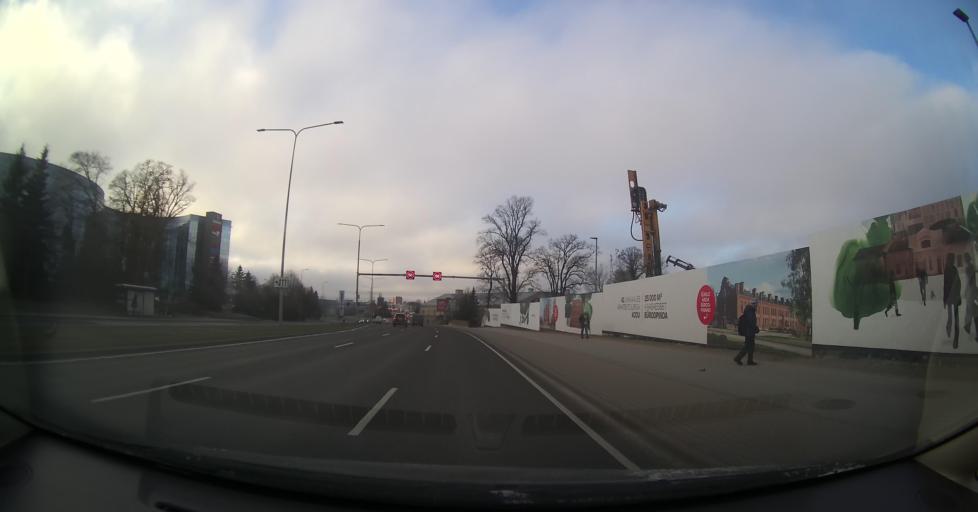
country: EE
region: Harju
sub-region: Tallinna linn
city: Tallinn
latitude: 59.4031
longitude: 24.7212
